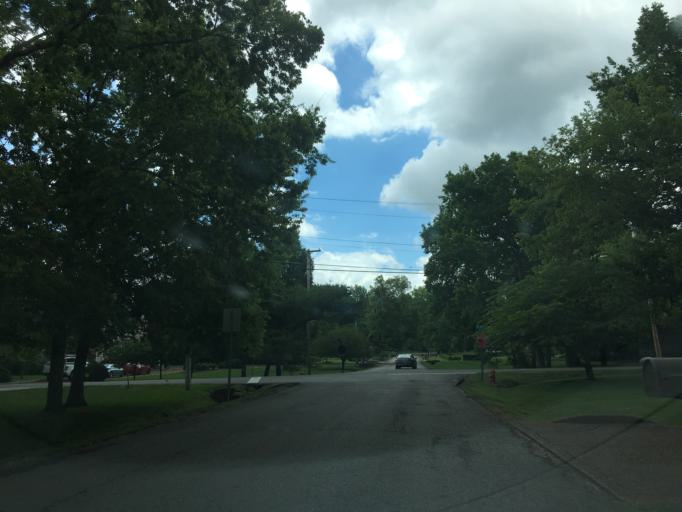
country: US
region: Tennessee
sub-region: Davidson County
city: Belle Meade
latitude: 36.0911
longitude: -86.8462
